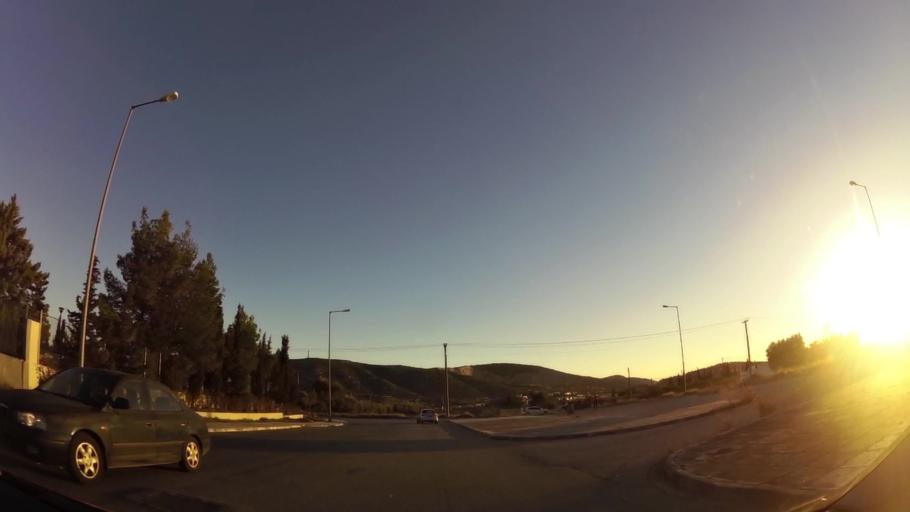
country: GR
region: Attica
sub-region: Nomarchia Dytikis Attikis
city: Ano Liosia
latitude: 38.0812
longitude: 23.6855
